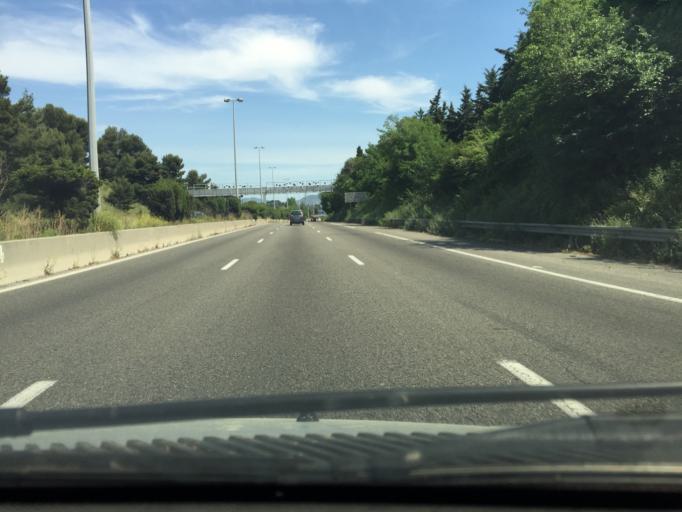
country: FR
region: Provence-Alpes-Cote d'Azur
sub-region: Departement des Bouches-du-Rhone
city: Marseille 11
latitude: 43.2942
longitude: 5.4689
